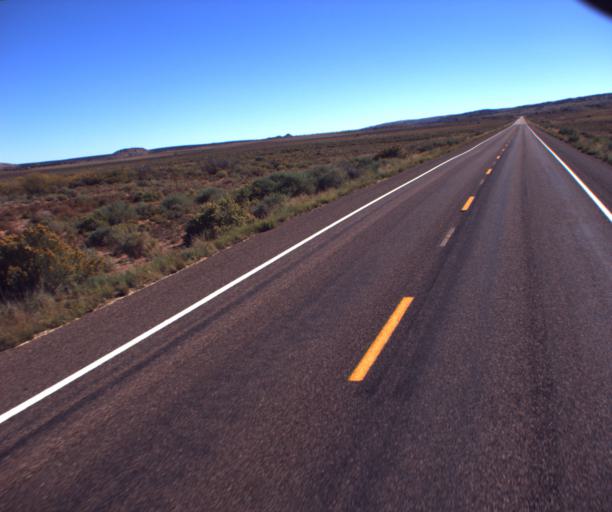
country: US
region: Arizona
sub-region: Apache County
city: Saint Johns
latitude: 34.5924
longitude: -109.6102
